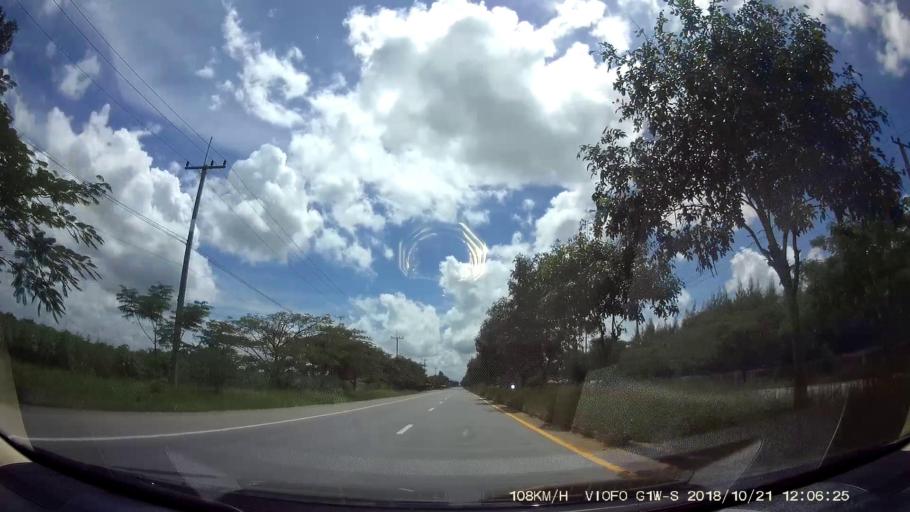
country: TH
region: Chaiyaphum
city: Chatturat
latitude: 15.4632
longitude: 101.8260
